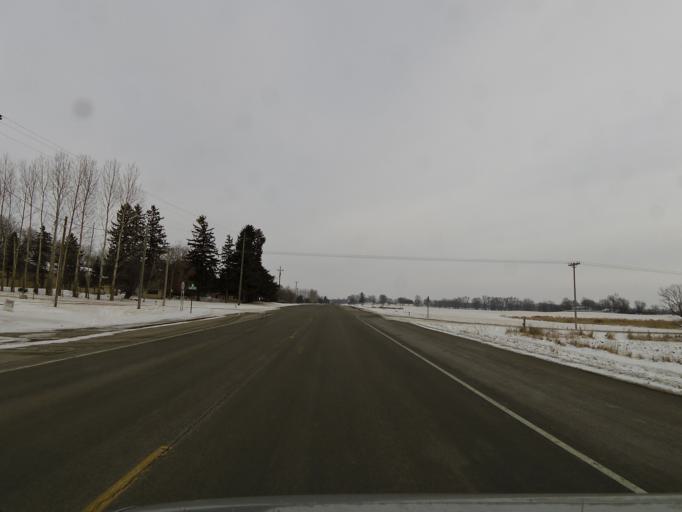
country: US
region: Minnesota
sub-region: McLeod County
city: Lester Prairie
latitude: 44.9064
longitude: -94.0949
